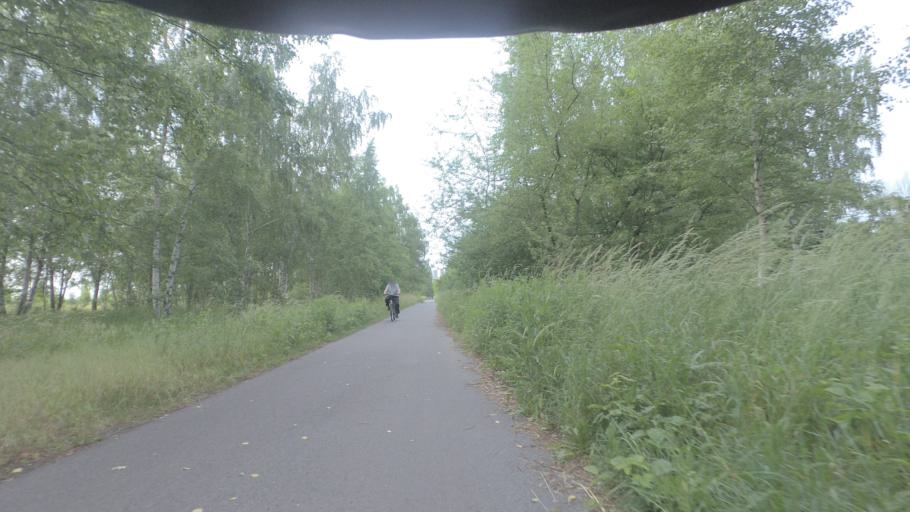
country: DE
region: Berlin
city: Gropiusstadt
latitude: 52.4169
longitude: 13.4687
